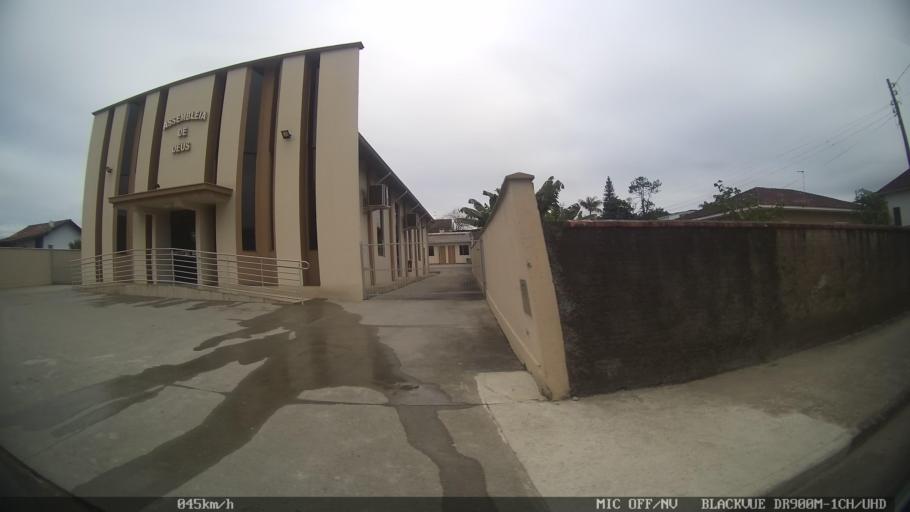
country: BR
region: Santa Catarina
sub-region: Joinville
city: Joinville
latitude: -26.3231
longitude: -48.9092
